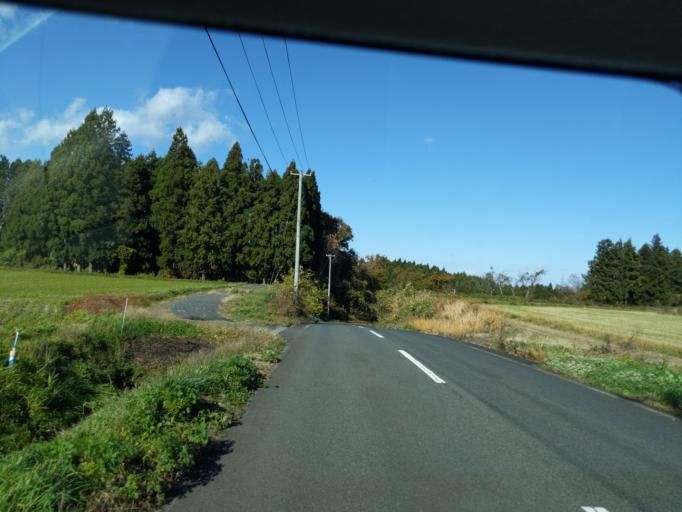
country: JP
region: Iwate
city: Mizusawa
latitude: 39.0809
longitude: 141.1214
